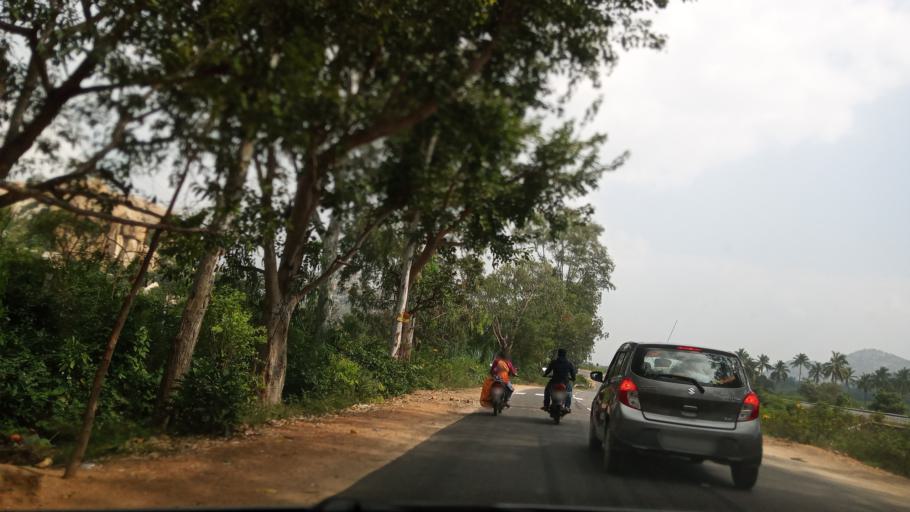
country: IN
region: Andhra Pradesh
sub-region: Chittoor
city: Madanapalle
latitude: 13.6354
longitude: 78.6057
